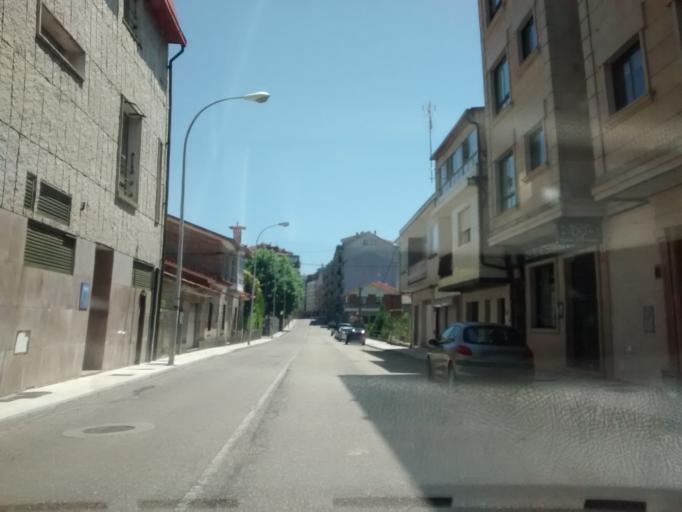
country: ES
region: Galicia
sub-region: Provincia de Pontevedra
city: Tui
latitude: 42.0510
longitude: -8.6496
